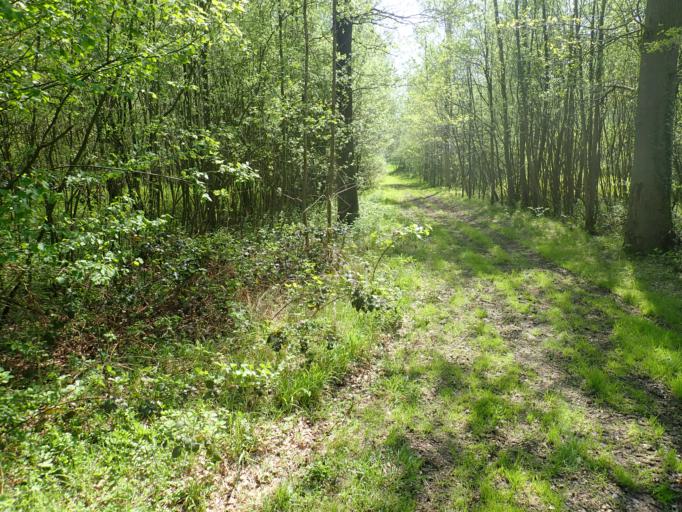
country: BE
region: Flanders
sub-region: Provincie Vlaams-Brabant
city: Merchtem
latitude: 50.9610
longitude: 4.2738
